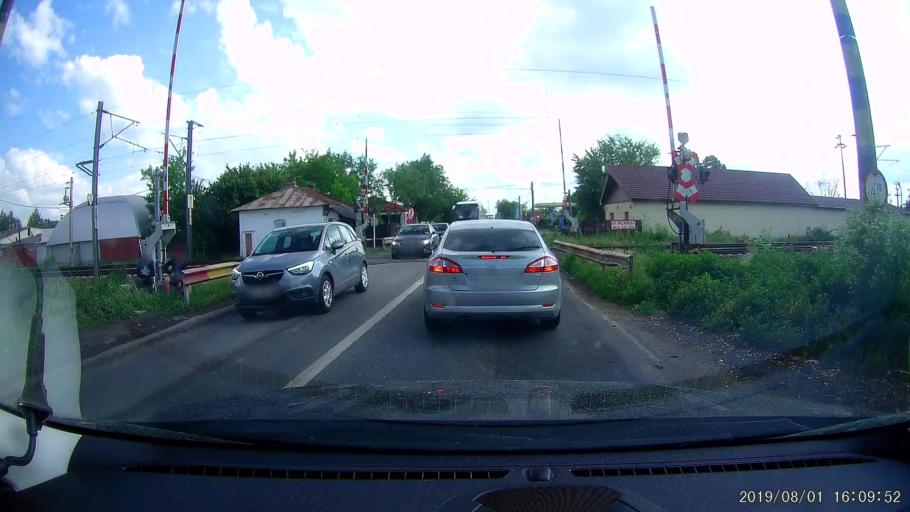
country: RO
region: Calarasi
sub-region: Comuna Dragalina
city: Drajna Noua
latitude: 44.4273
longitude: 27.3765
